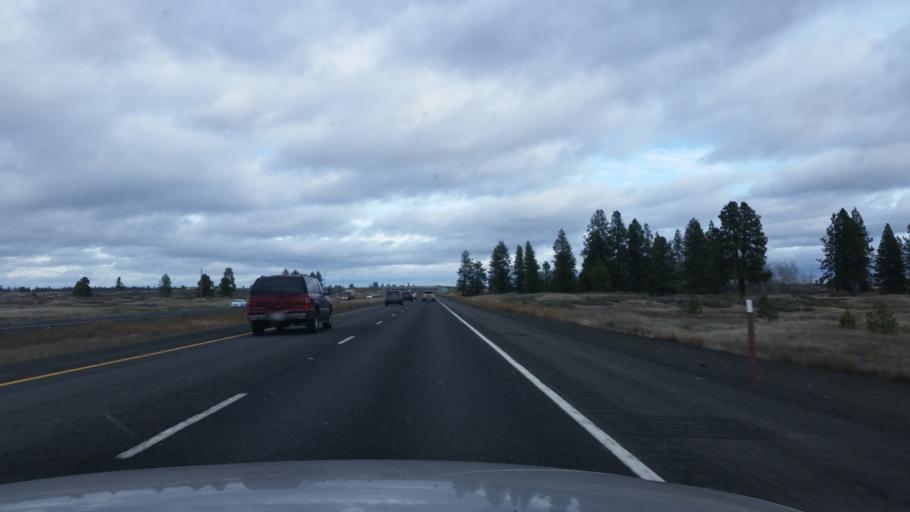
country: US
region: Washington
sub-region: Spokane County
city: Medical Lake
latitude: 47.3897
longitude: -117.8501
